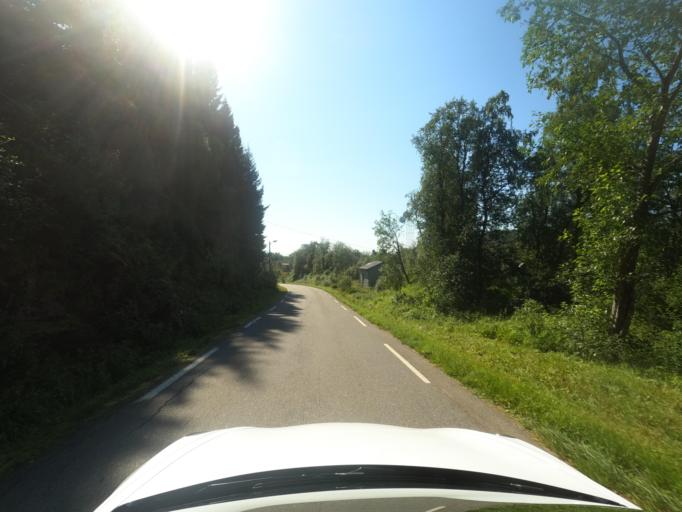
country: NO
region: Nordland
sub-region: Hadsel
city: Stokmarknes
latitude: 68.3053
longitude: 15.0935
